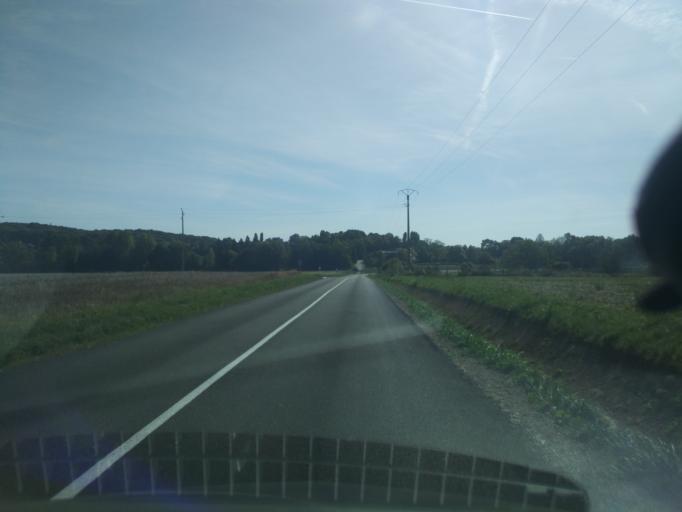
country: FR
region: Ile-de-France
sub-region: Departement de l'Essonne
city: Briis-sous-Forges
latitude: 48.6308
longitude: 2.1145
